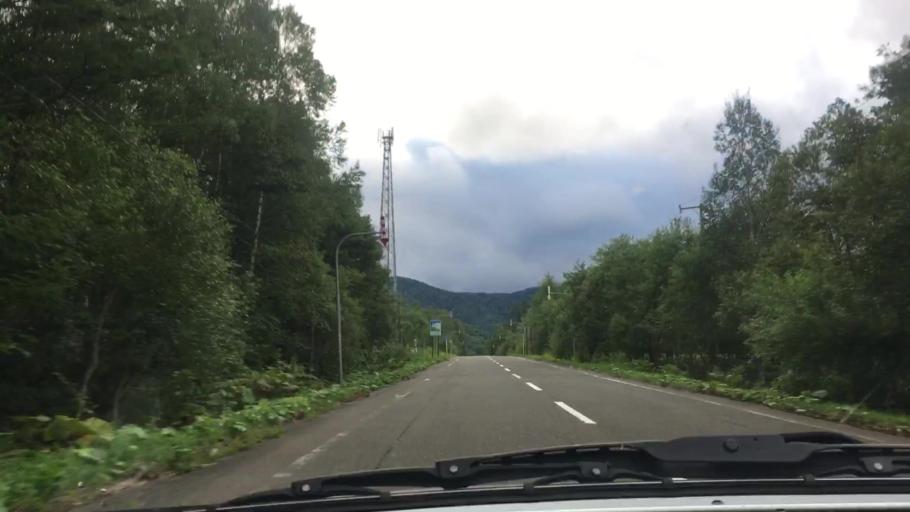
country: JP
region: Hokkaido
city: Shimo-furano
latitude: 43.0492
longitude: 142.6672
